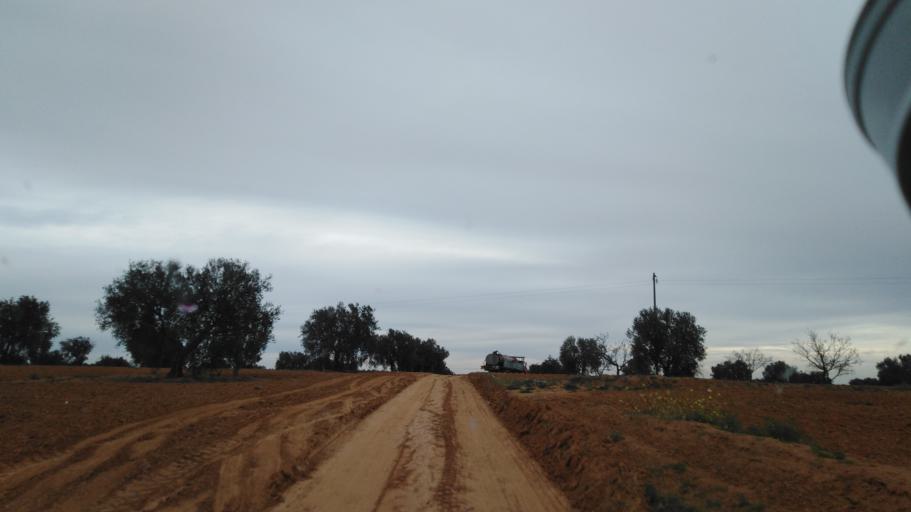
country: TN
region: Safaqis
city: Bi'r `Ali Bin Khalifah
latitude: 34.7718
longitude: 10.3733
